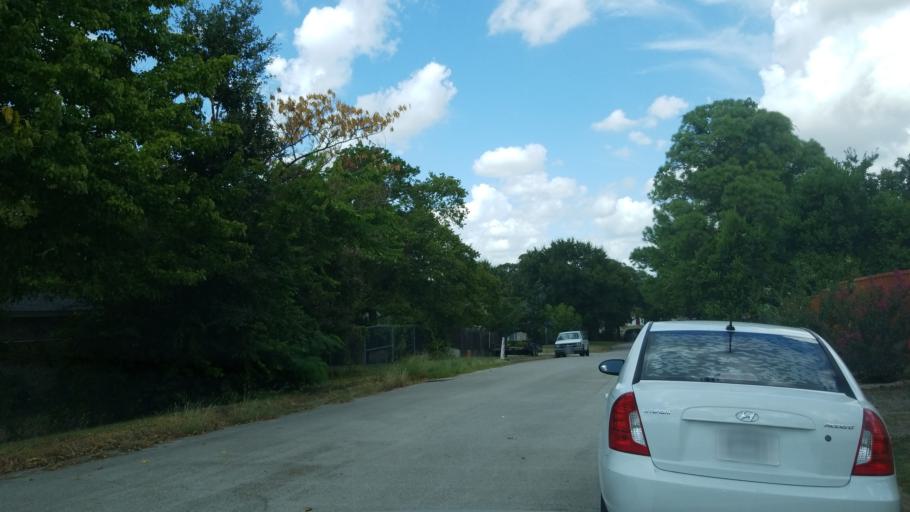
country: US
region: Texas
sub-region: Tarrant County
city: Euless
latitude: 32.8571
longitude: -97.0930
